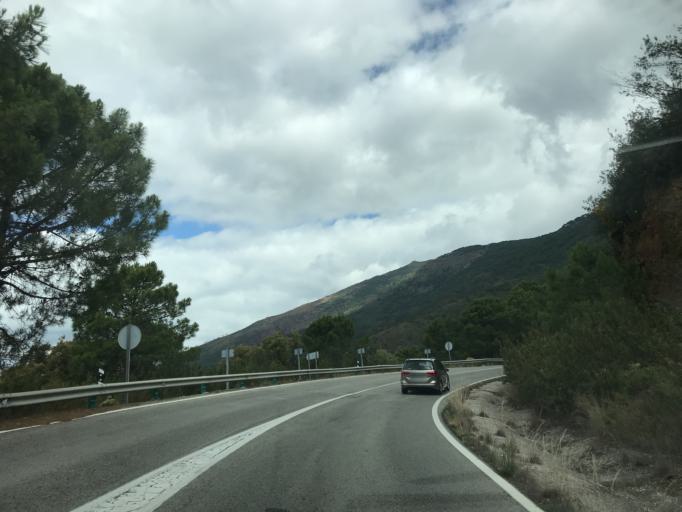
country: ES
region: Andalusia
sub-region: Provincia de Malaga
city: Benahavis
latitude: 36.5448
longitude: -5.0236
